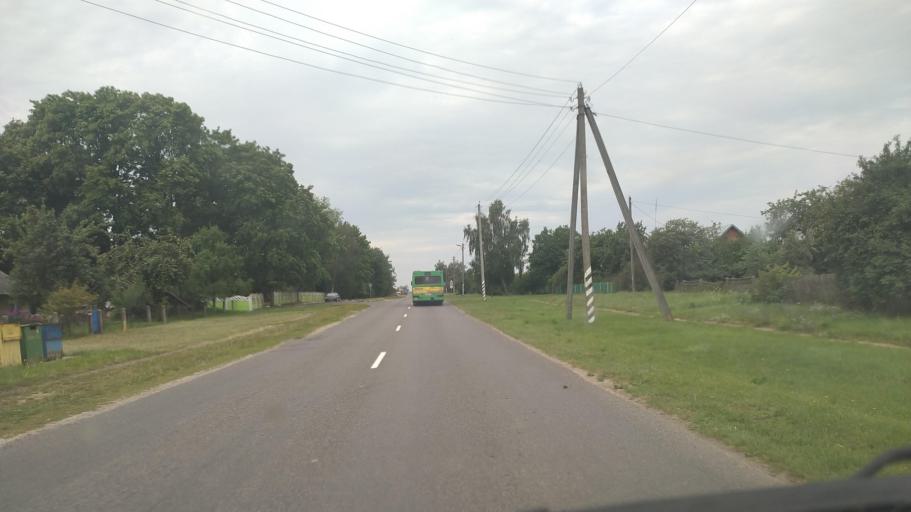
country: BY
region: Brest
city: Byaroza
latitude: 52.5803
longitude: 24.8585
